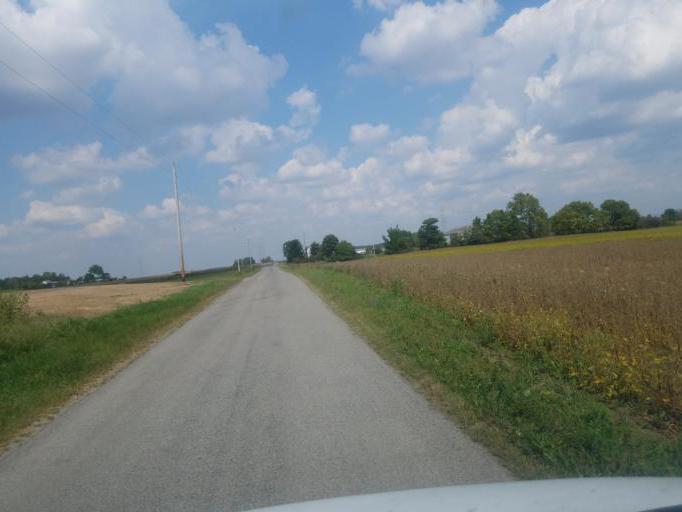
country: US
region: Ohio
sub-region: Hardin County
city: Ada
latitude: 40.6200
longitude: -83.7868
